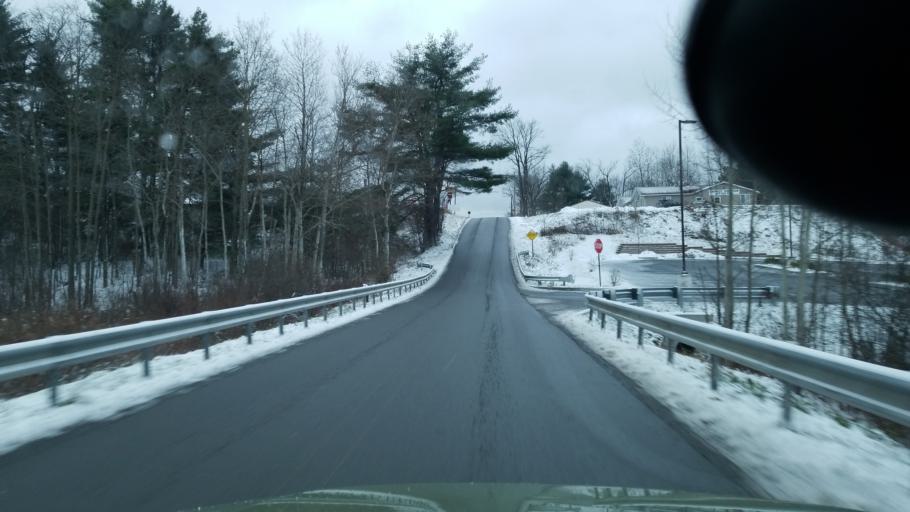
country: US
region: Pennsylvania
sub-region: Clearfield County
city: DuBois
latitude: 41.1252
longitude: -78.7368
